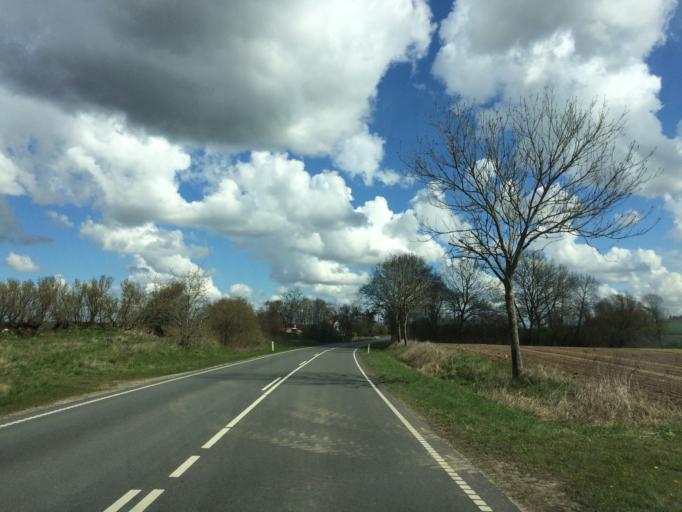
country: DK
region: South Denmark
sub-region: Assens Kommune
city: Harby
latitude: 55.2265
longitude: 10.1762
